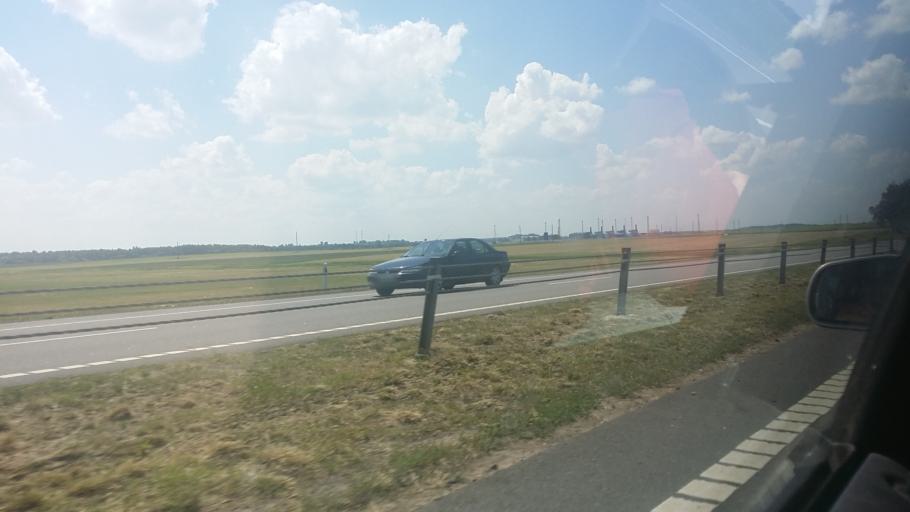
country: BY
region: Minsk
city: Luhavaya Slabada
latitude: 53.7614
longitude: 27.8919
